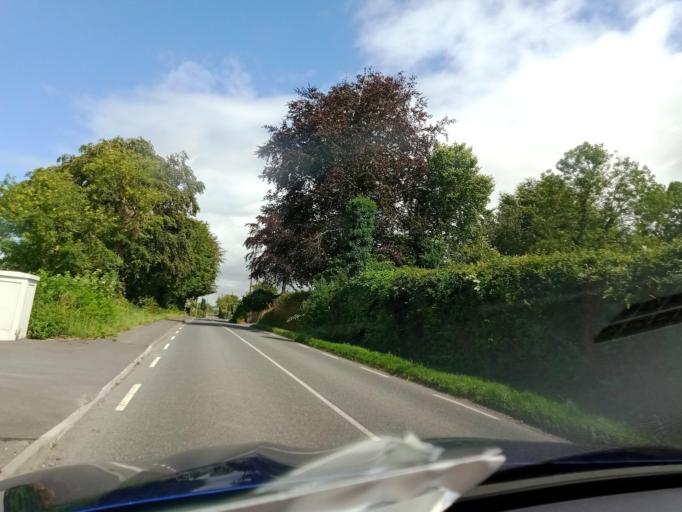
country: IE
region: Leinster
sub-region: Laois
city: Abbeyleix
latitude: 52.9258
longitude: -7.3314
